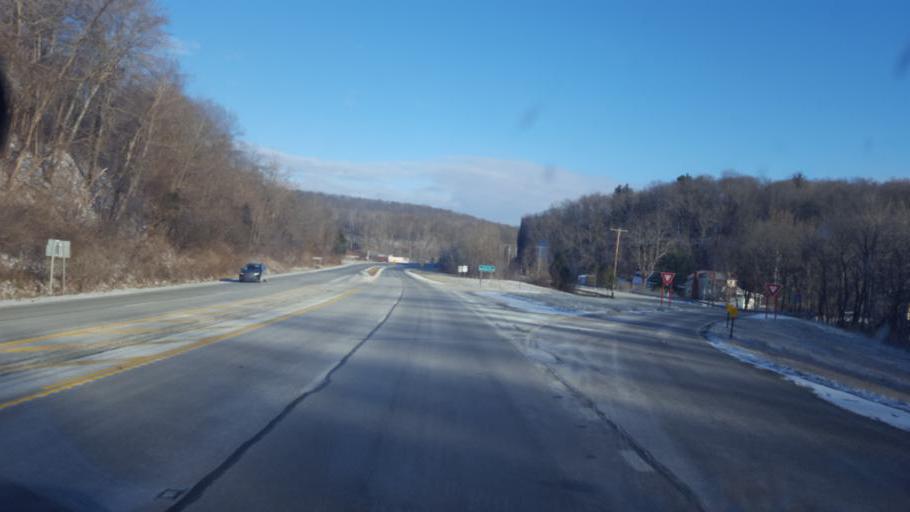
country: US
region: Ohio
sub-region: Ross County
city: Chillicothe
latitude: 39.2419
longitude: -82.9835
